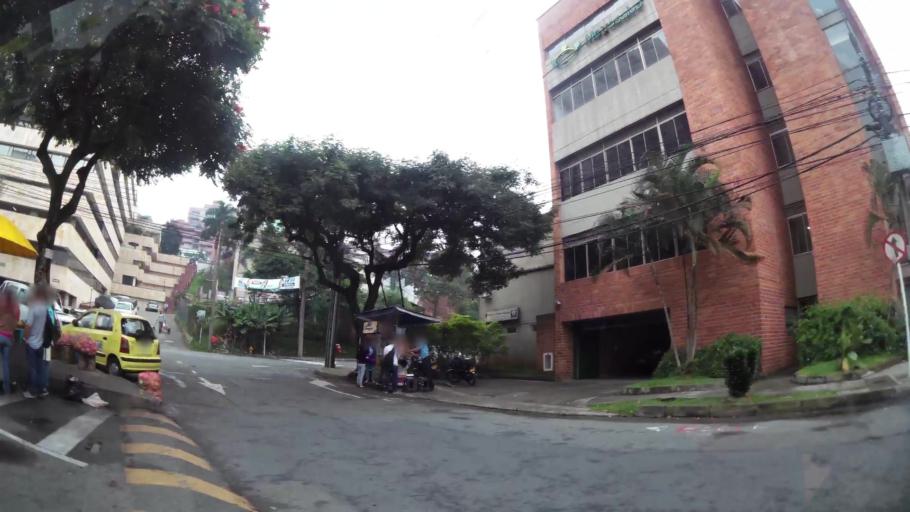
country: CO
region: Antioquia
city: Medellin
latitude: 6.2148
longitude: -75.5711
